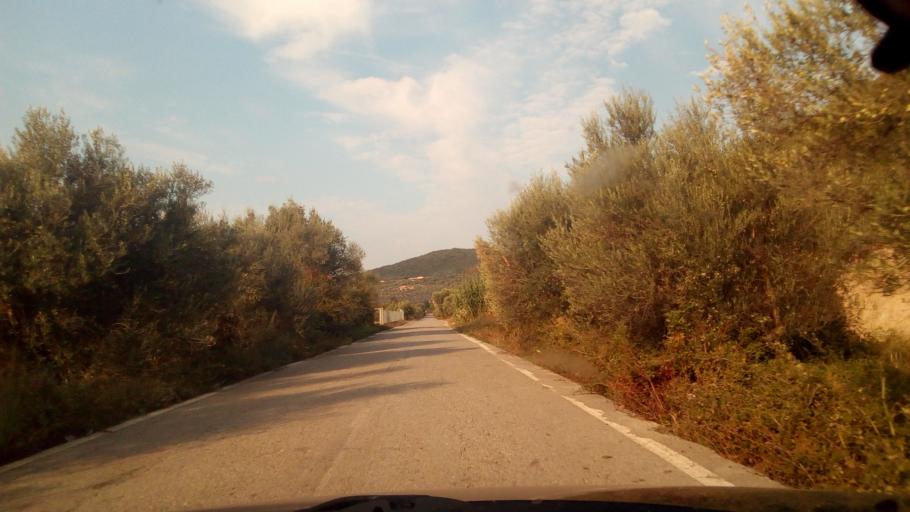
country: GR
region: West Greece
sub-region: Nomos Aitolias kai Akarnanias
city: Nafpaktos
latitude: 38.4240
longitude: 21.9236
